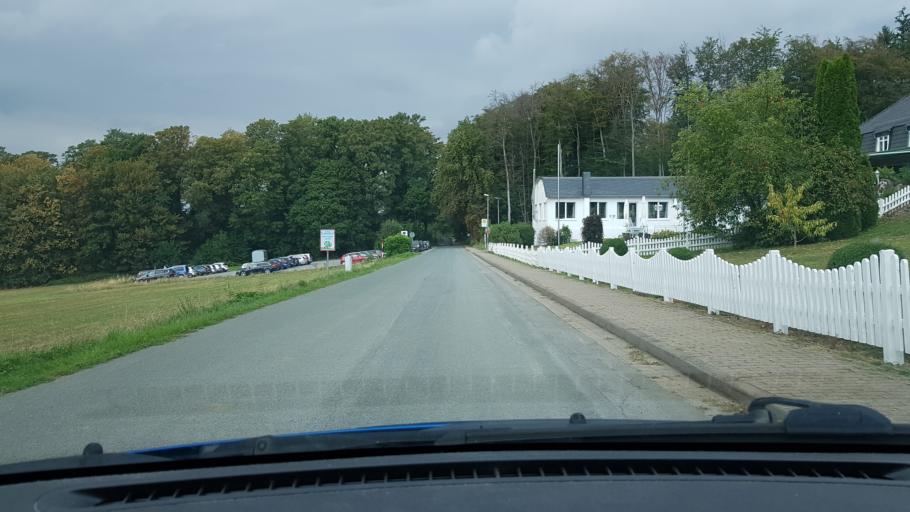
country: DE
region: Lower Saxony
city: Bad Munder am Deister
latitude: 52.2106
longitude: 9.4822
